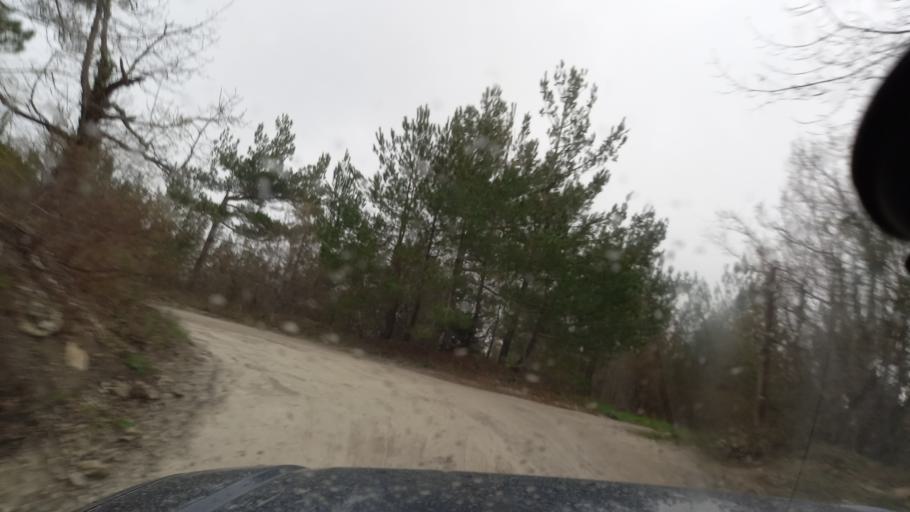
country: RU
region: Krasnodarskiy
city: Dzhubga
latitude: 44.3199
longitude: 38.6786
